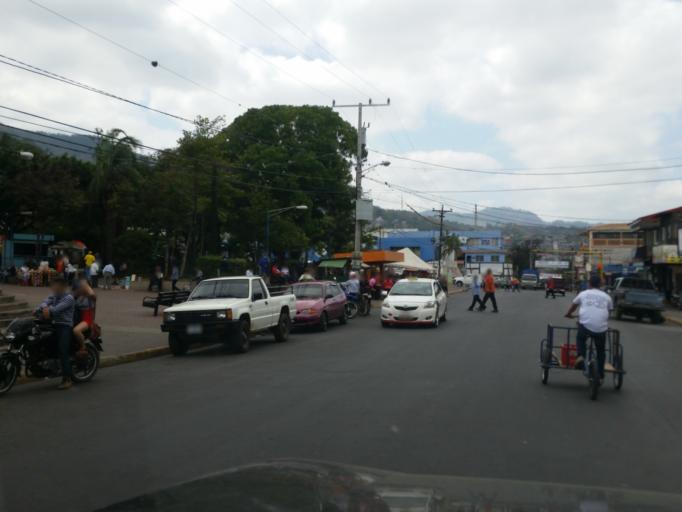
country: NI
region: Matagalpa
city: Matagalpa
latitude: 12.9287
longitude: -85.9188
